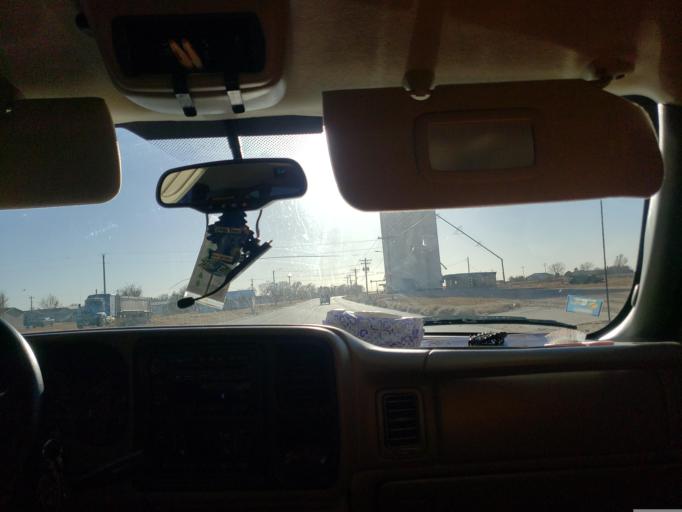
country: US
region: Kansas
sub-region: Stevens County
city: Hugoton
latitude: 37.3253
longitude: -101.2093
